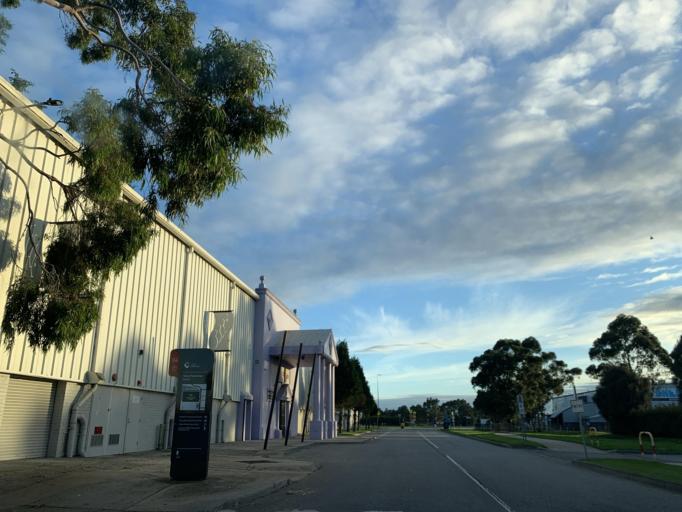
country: AU
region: Victoria
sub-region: Casey
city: Cranbourne East
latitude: -38.1136
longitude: 145.2967
